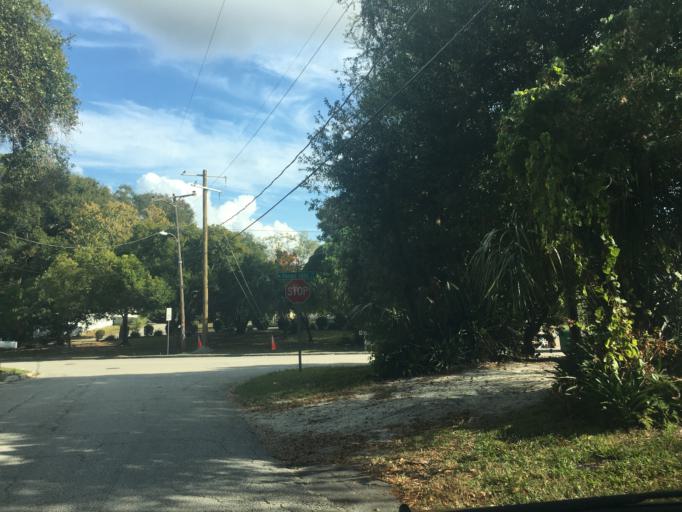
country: US
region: Florida
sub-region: Hillsborough County
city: Egypt Lake-Leto
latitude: 27.9968
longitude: -82.4745
